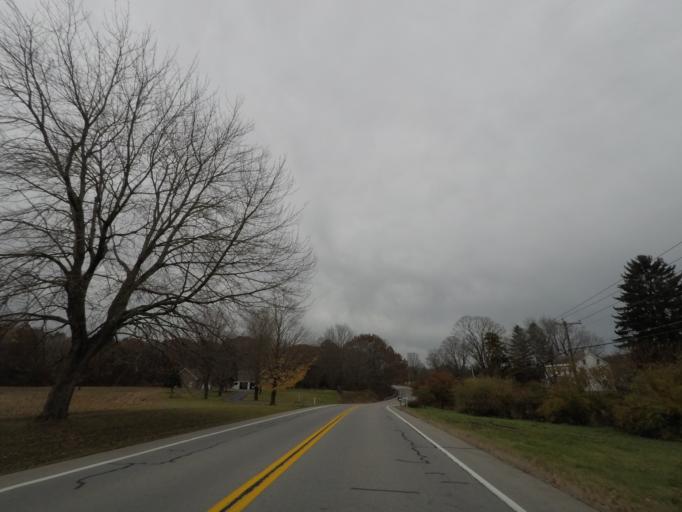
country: US
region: New York
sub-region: Schenectady County
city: Niskayuna
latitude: 42.8210
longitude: -73.8257
